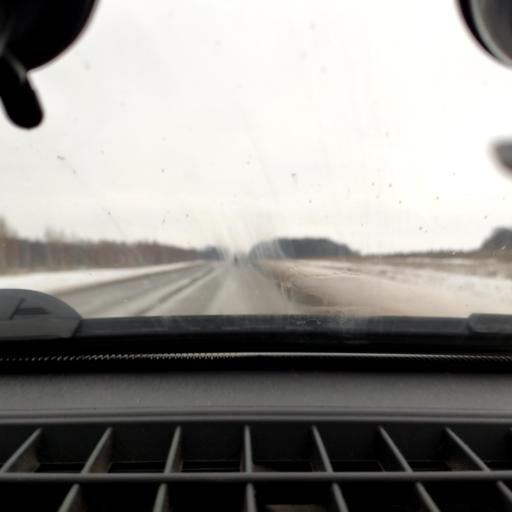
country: RU
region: Bashkortostan
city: Iglino
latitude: 54.7790
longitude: 56.4165
